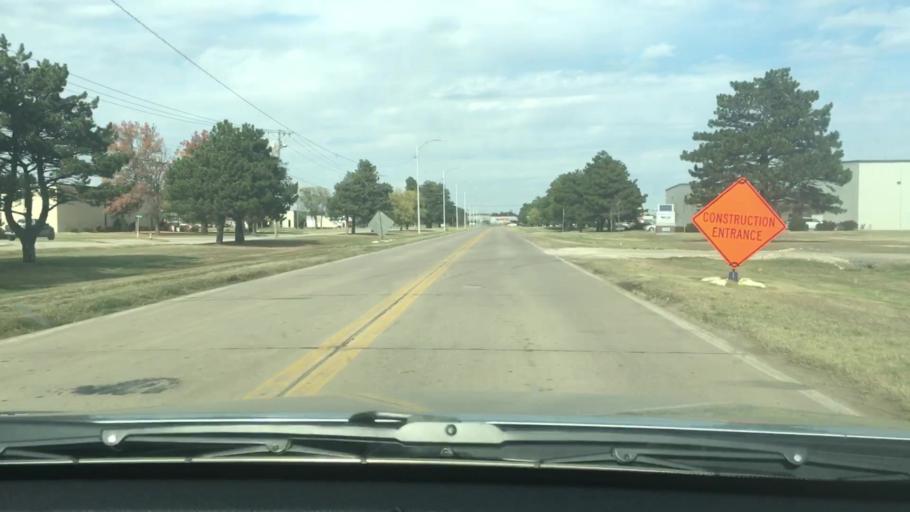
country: US
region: Kansas
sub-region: Sedgwick County
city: Wichita
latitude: 37.6669
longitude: -97.4211
